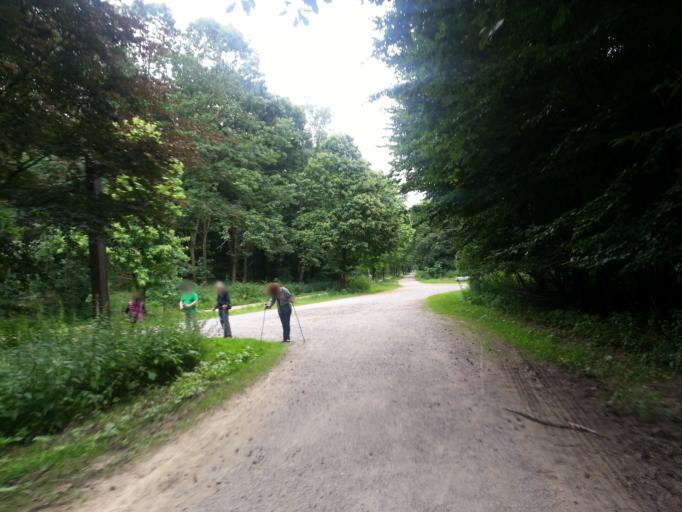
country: DE
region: North Rhine-Westphalia
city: Oer-Erkenschwick
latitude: 51.6801
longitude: 7.2238
